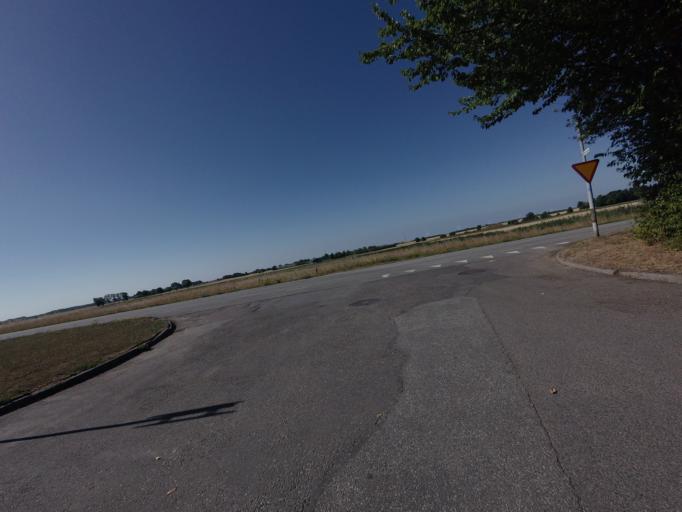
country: SE
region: Skane
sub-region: Trelleborgs Kommun
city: Skare
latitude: 55.4026
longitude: 13.0832
